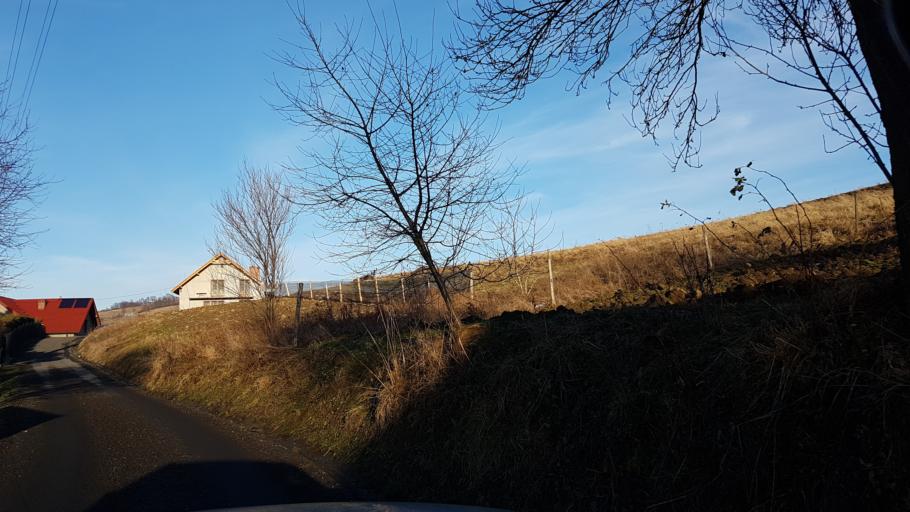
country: PL
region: Lesser Poland Voivodeship
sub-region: Powiat nowosadecki
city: Rytro
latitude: 49.4972
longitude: 20.6604
